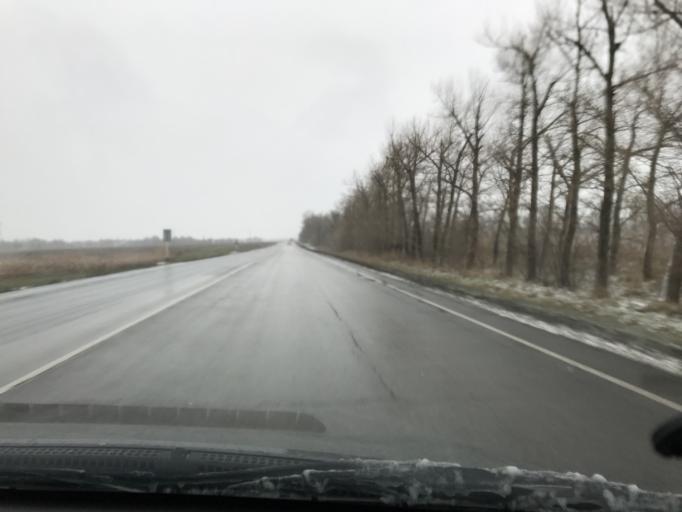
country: RU
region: Rostov
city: Mechetinskaya
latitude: 46.6651
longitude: 40.5447
